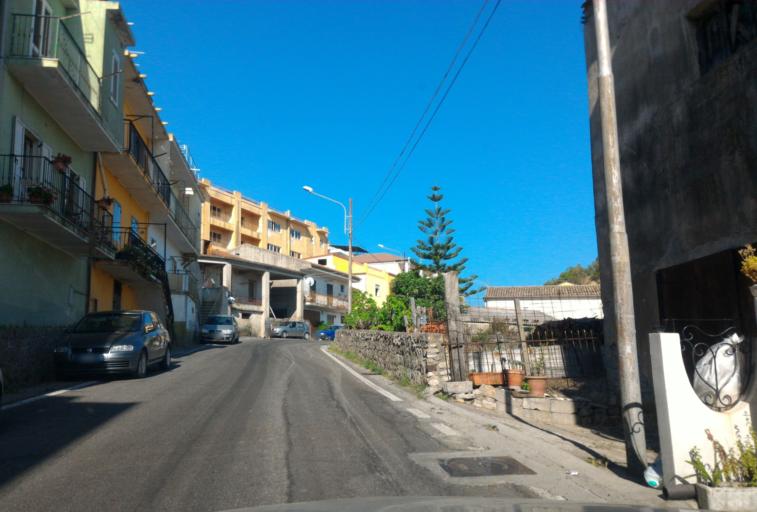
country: IT
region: Calabria
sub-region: Provincia di Crotone
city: Ciro
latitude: 39.3820
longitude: 17.0643
